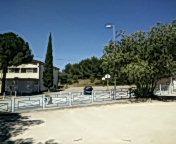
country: FR
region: Languedoc-Roussillon
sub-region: Departement du Gard
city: Uchaud
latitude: 43.7602
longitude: 4.2652
